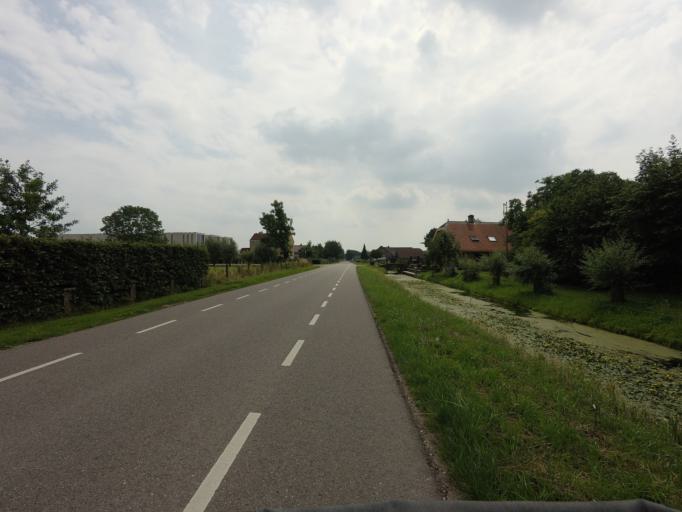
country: NL
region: Utrecht
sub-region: Gemeente Vianen
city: Vianen
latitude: 52.0053
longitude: 5.1262
